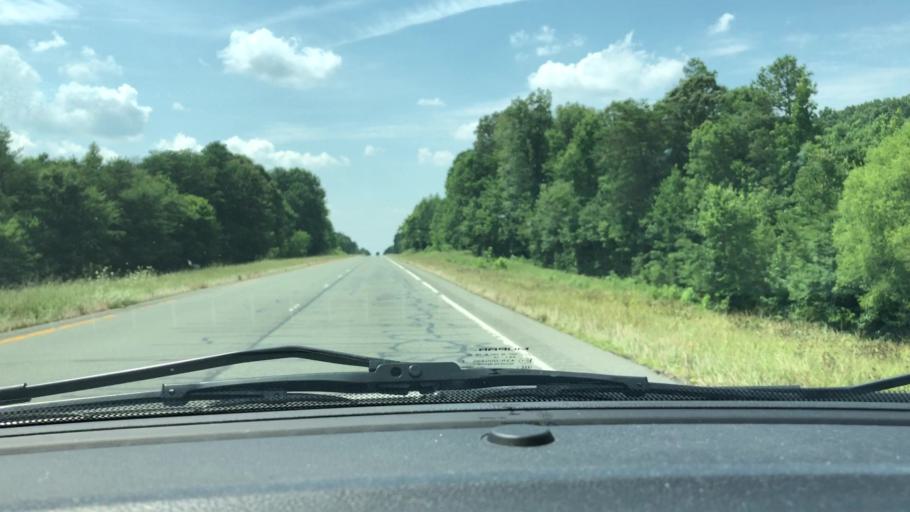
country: US
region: North Carolina
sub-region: Chatham County
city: Siler City
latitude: 35.7732
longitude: -79.4914
